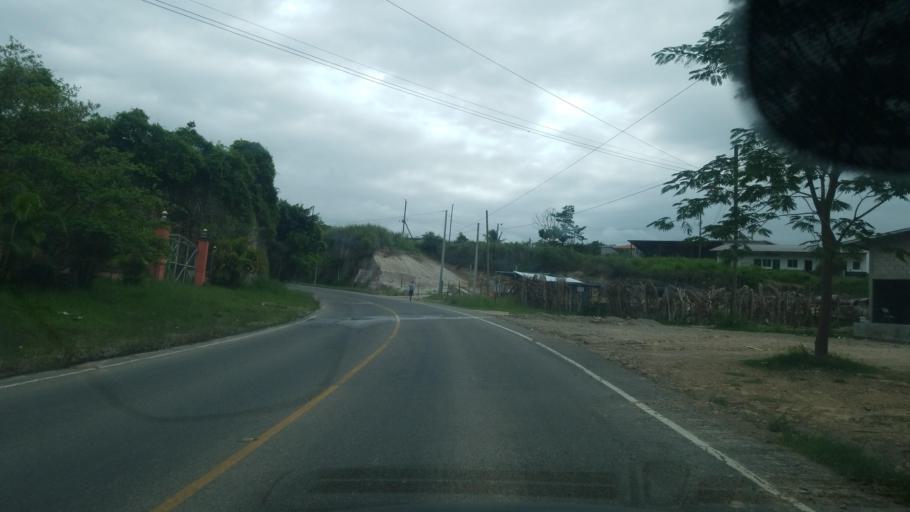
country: HN
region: Ocotepeque
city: Lucerna
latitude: 14.5599
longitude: -88.9379
